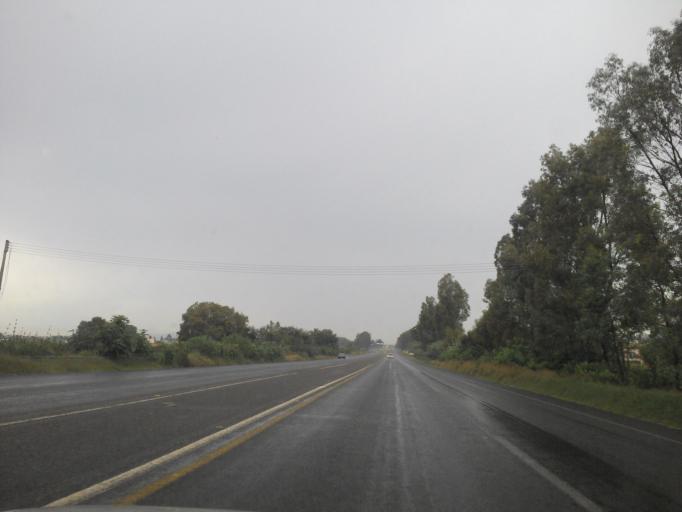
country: MX
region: Jalisco
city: Tepatitlan de Morelos
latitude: 20.8815
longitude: -102.6956
